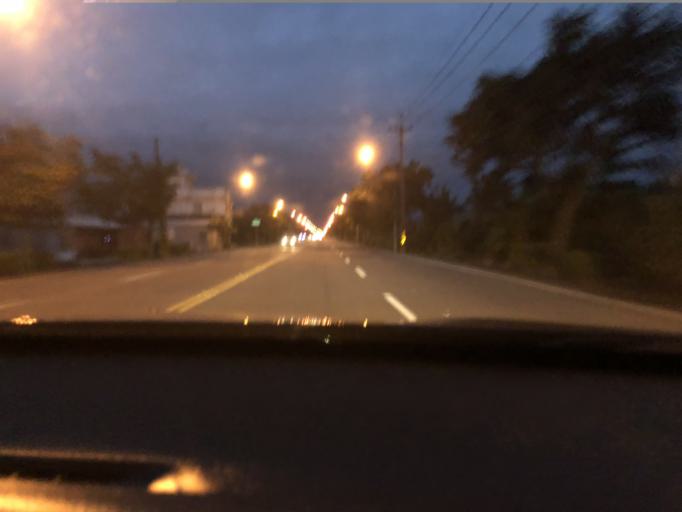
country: TW
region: Taiwan
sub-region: Hualien
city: Hualian
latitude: 23.9512
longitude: 121.5612
